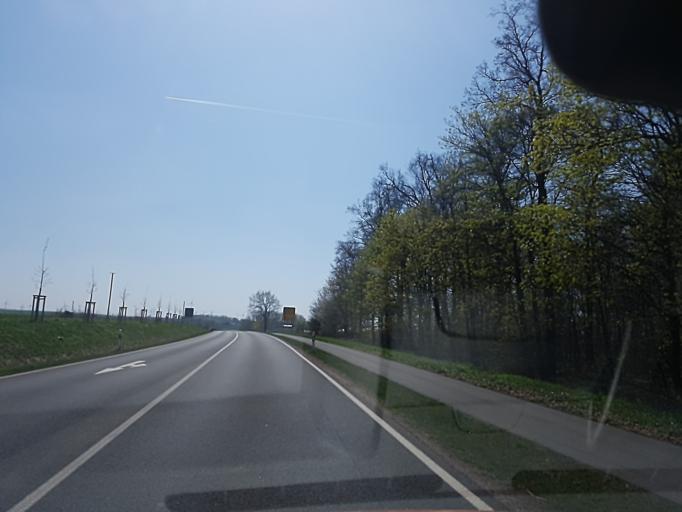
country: DE
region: Saxony
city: Mutzschen
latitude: 51.2691
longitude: 12.9211
